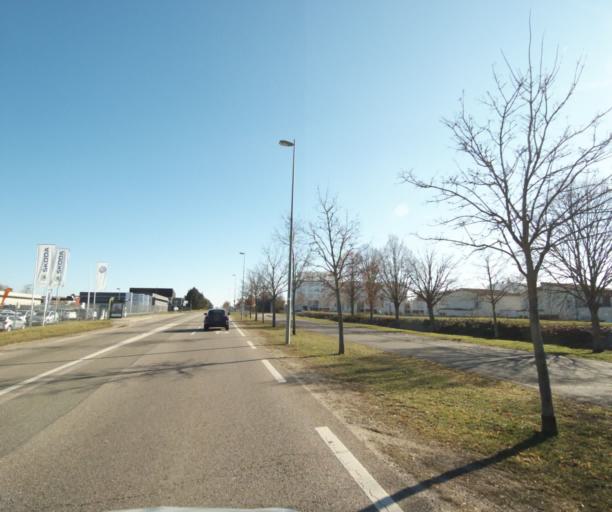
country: FR
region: Lorraine
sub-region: Departement de Meurthe-et-Moselle
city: Tomblaine
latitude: 48.6903
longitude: 6.2147
